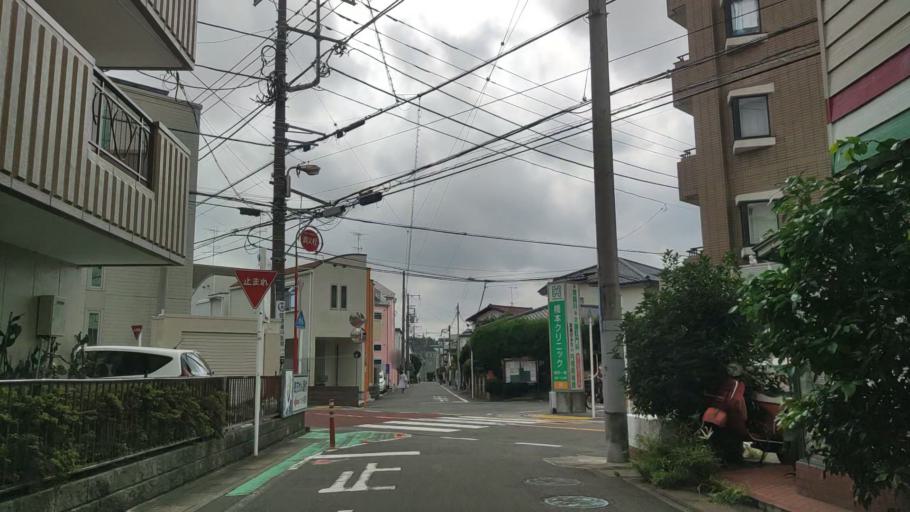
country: JP
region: Kanagawa
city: Minami-rinkan
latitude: 35.5068
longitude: 139.4426
